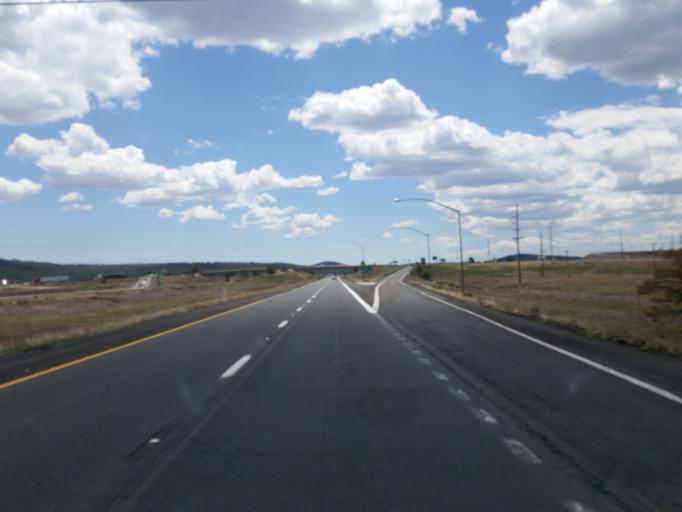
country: US
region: Arizona
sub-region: Coconino County
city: Parks
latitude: 35.2383
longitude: -111.8276
